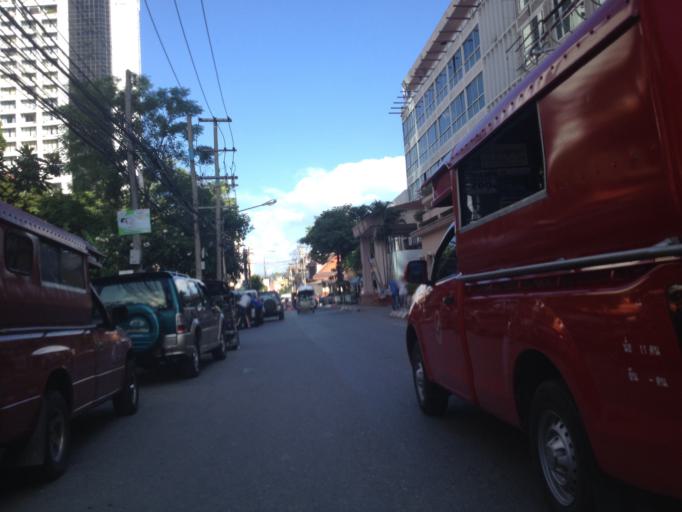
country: TH
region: Chiang Mai
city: Chiang Mai
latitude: 18.7841
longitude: 98.9994
